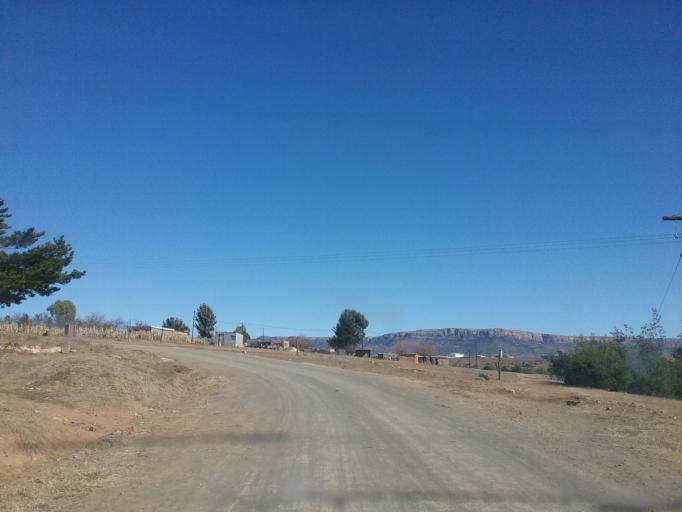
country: LS
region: Maseru
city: Maseru
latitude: -29.4502
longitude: 27.5783
